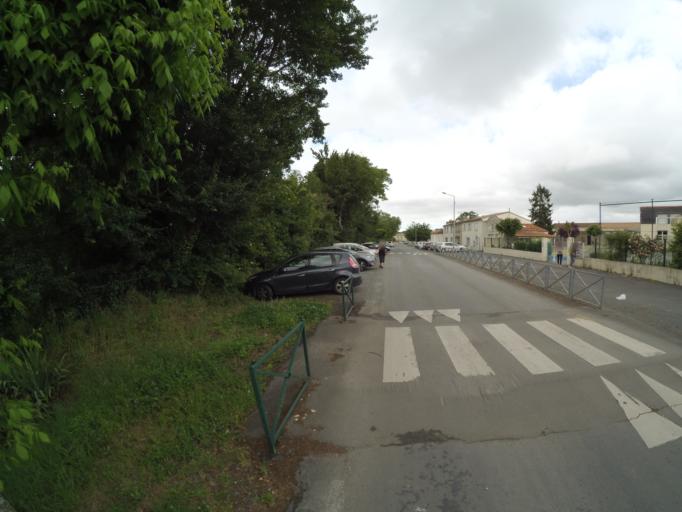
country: FR
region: Poitou-Charentes
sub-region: Departement de la Charente-Maritime
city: Saint-Laurent-de-la-Pree
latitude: 45.9918
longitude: -1.0234
